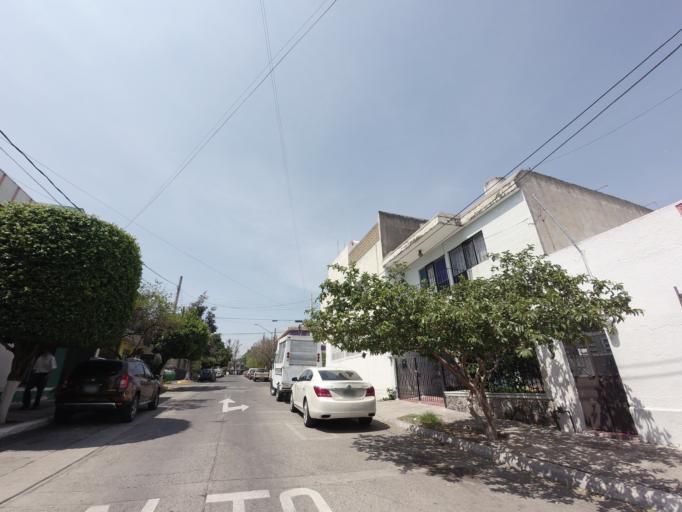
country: MX
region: Jalisco
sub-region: Zapopan
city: Zapopan
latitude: 20.6917
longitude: -103.3445
